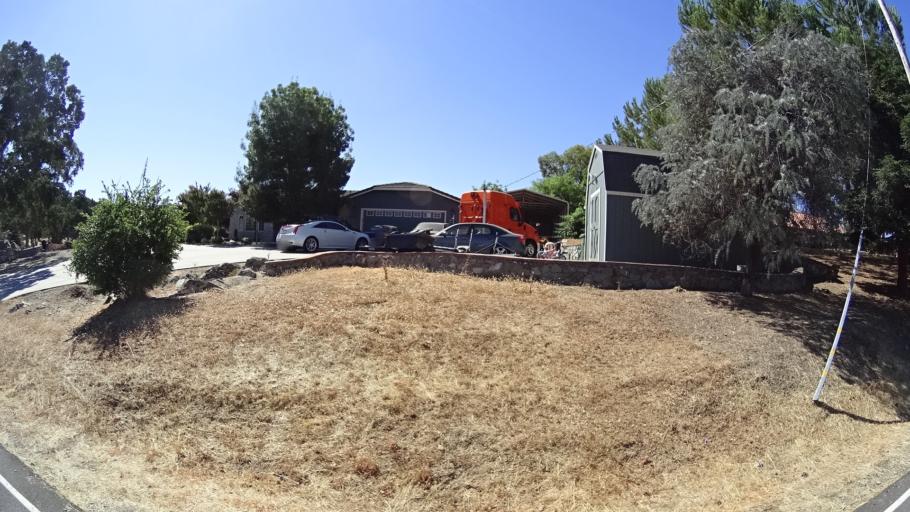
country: US
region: California
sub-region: Calaveras County
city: Rancho Calaveras
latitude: 38.1019
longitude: -120.8751
